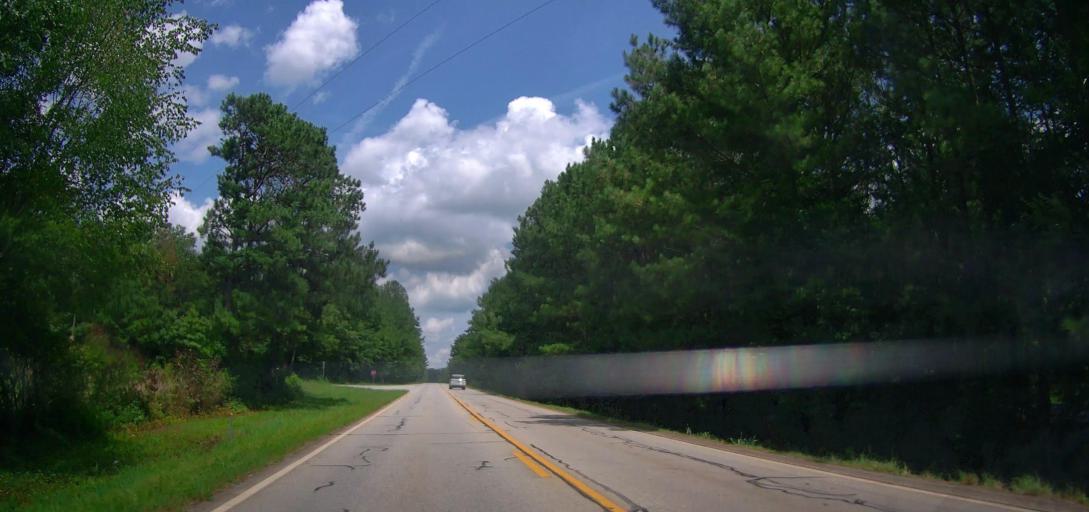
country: US
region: Georgia
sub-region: Troup County
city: Hogansville
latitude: 33.2327
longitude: -84.9582
